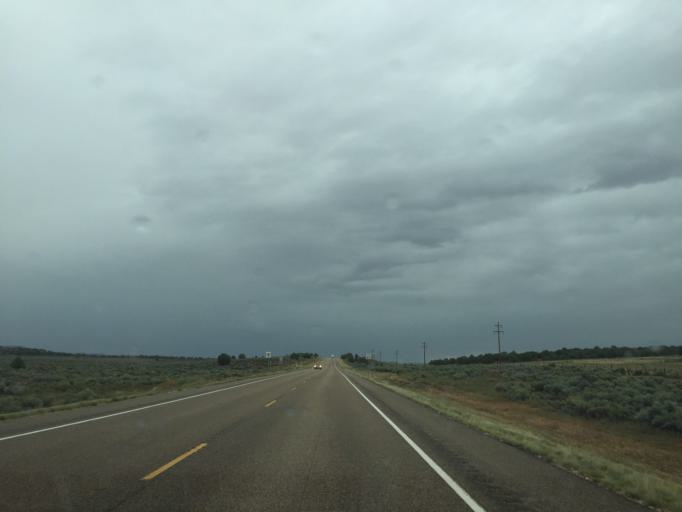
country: US
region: Utah
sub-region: Kane County
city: Kanab
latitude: 37.1405
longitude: -112.0765
